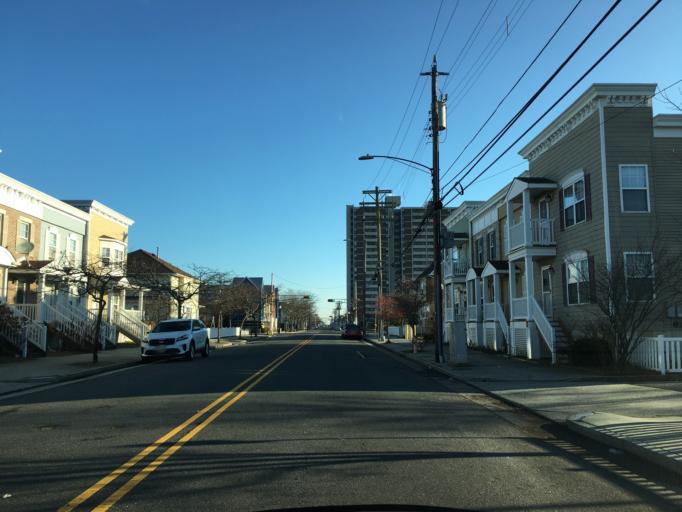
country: US
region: New Jersey
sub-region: Atlantic County
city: Atlantic City
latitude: 39.3675
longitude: -74.4280
